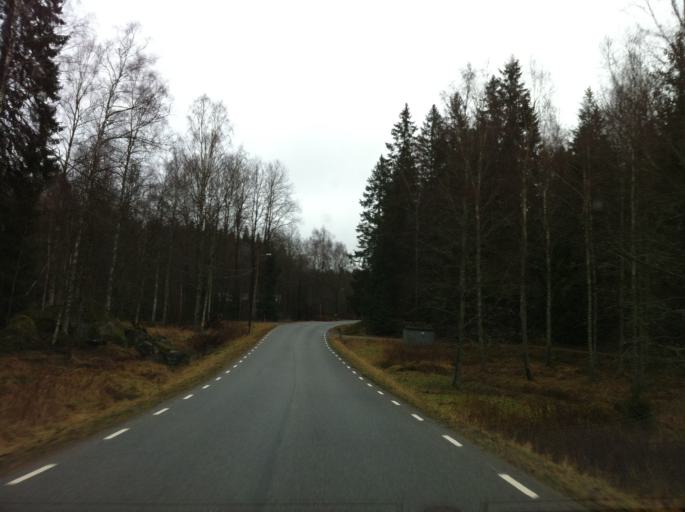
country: SE
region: Blekinge
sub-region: Olofstroms Kommun
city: Olofstroem
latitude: 56.3607
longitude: 14.5014
